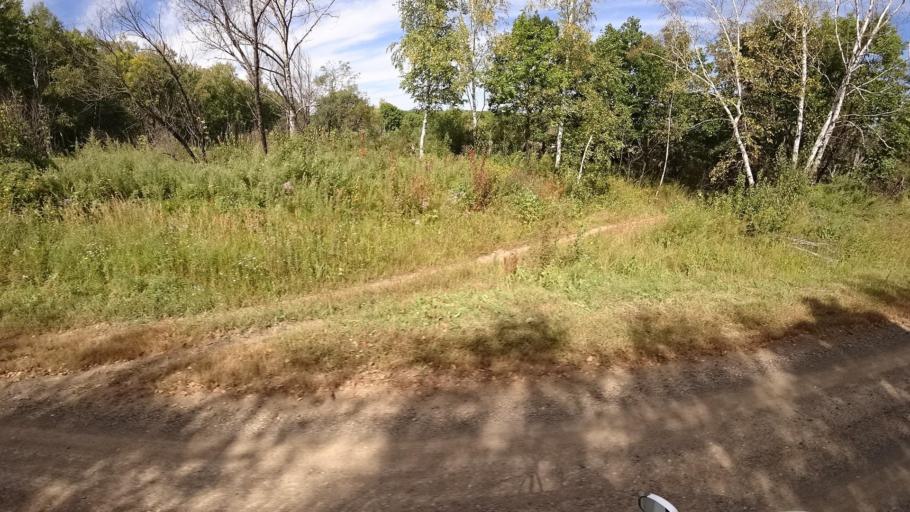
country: RU
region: Primorskiy
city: Yakovlevka
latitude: 44.7015
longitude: 133.6464
